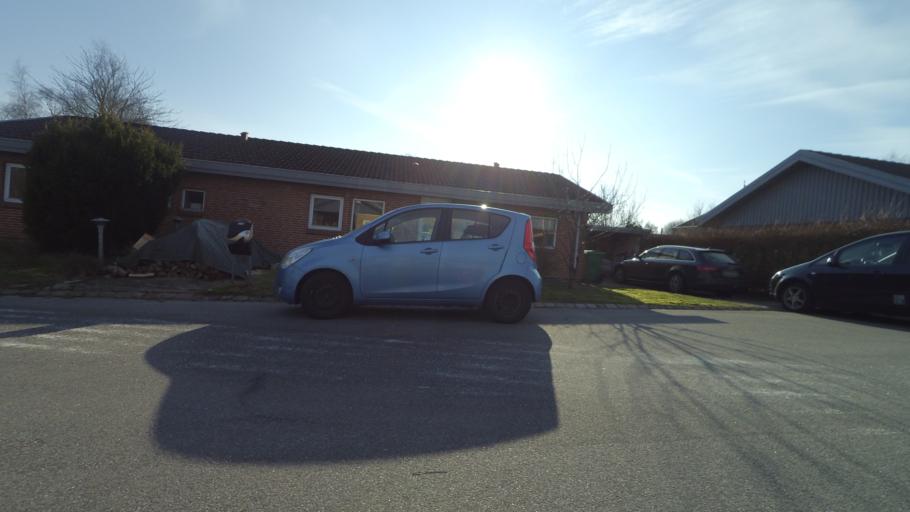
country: DK
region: Central Jutland
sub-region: Arhus Kommune
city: Kolt
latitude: 56.1097
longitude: 10.0864
